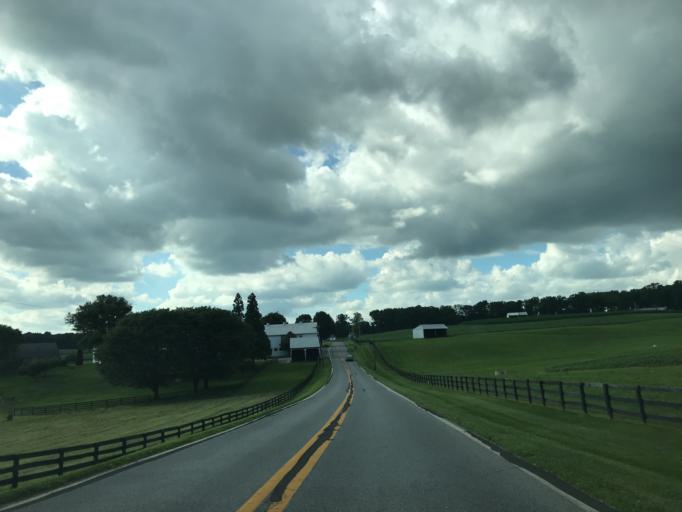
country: US
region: Maryland
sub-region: Carroll County
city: Manchester
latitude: 39.6733
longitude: -76.8212
